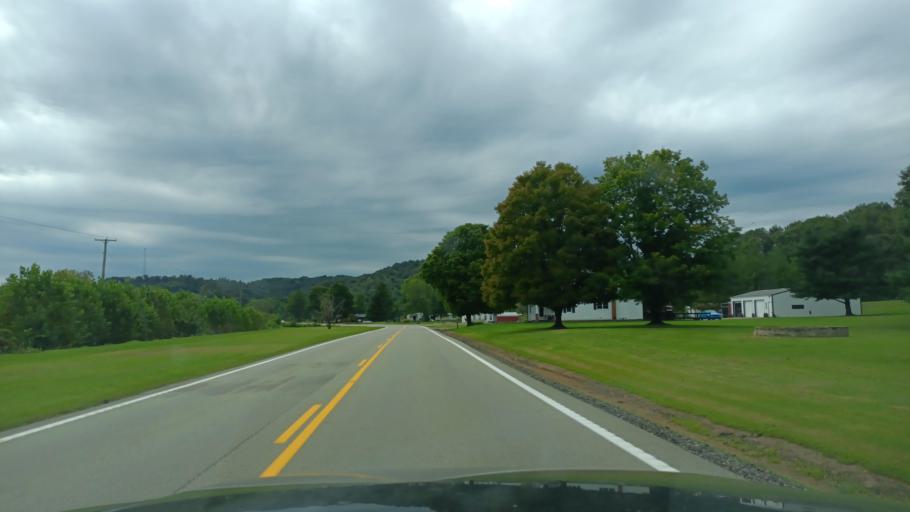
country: US
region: Ohio
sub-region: Vinton County
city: McArthur
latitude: 39.2707
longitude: -82.6699
